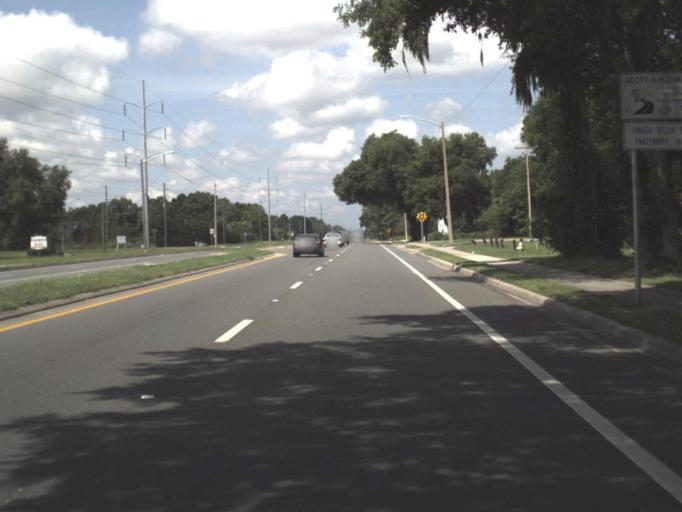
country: US
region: Florida
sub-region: Alachua County
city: Gainesville
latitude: 29.5985
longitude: -82.4222
